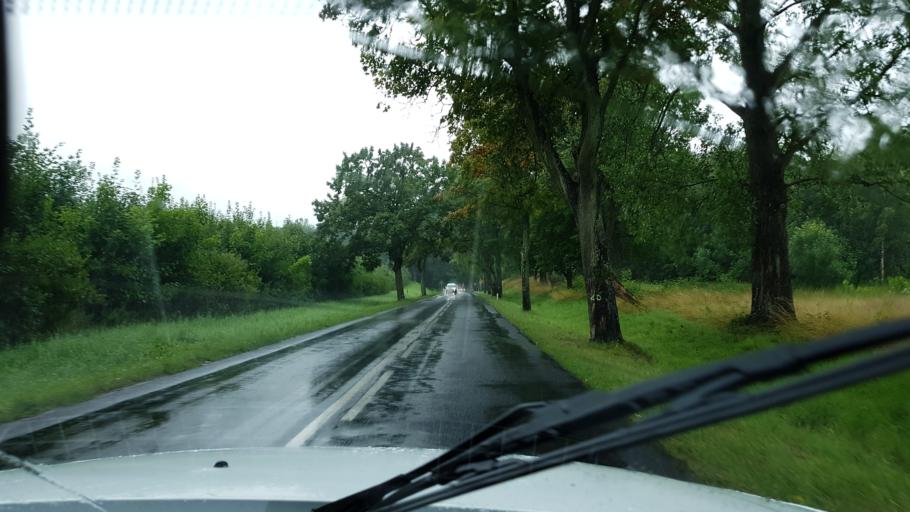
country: PL
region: West Pomeranian Voivodeship
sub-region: Powiat goleniowski
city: Nowogard
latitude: 53.5976
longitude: 15.1550
